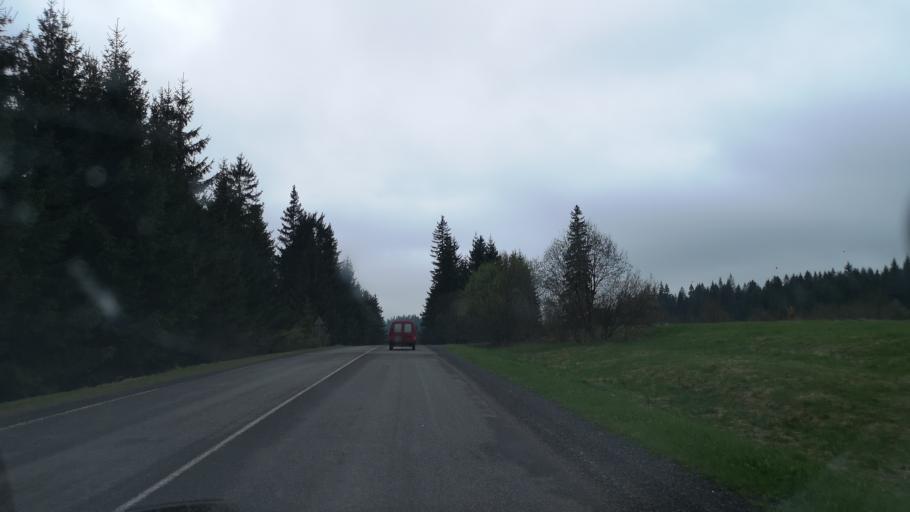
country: SK
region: Zilinsky
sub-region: Okres Liptovsky Mikulas
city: Hybe
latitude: 49.0661
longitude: 19.9340
